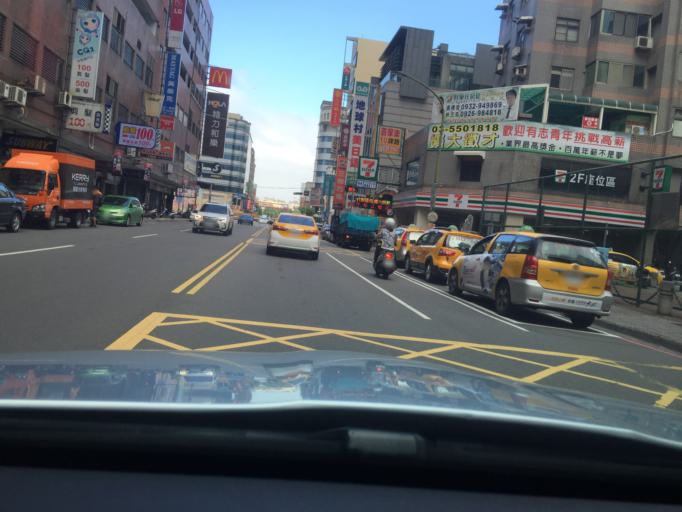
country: TW
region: Taiwan
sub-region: Hsinchu
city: Zhubei
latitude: 24.8261
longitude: 121.0092
